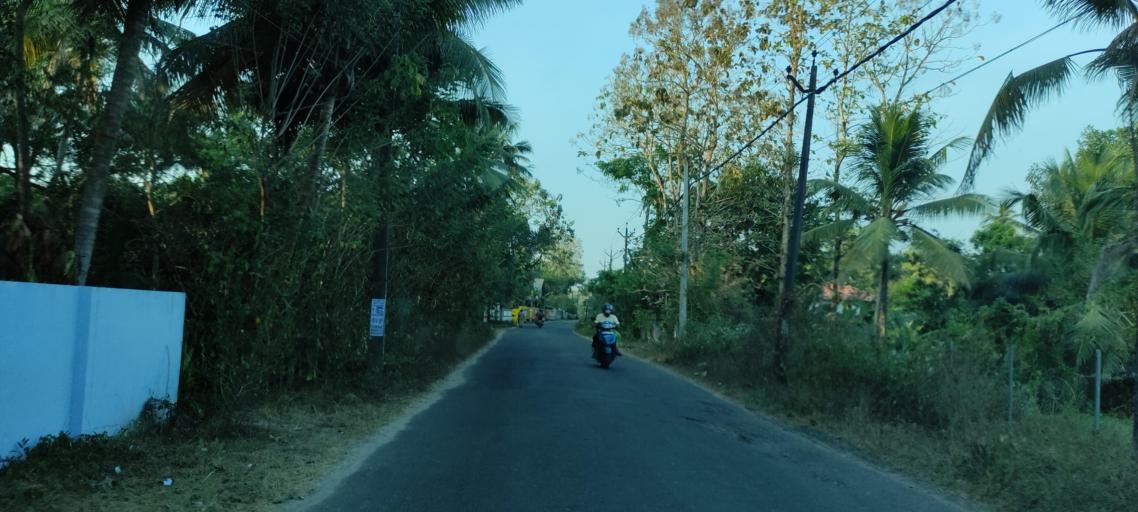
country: IN
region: Kerala
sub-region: Alappuzha
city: Kutiatodu
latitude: 9.7621
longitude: 76.3533
